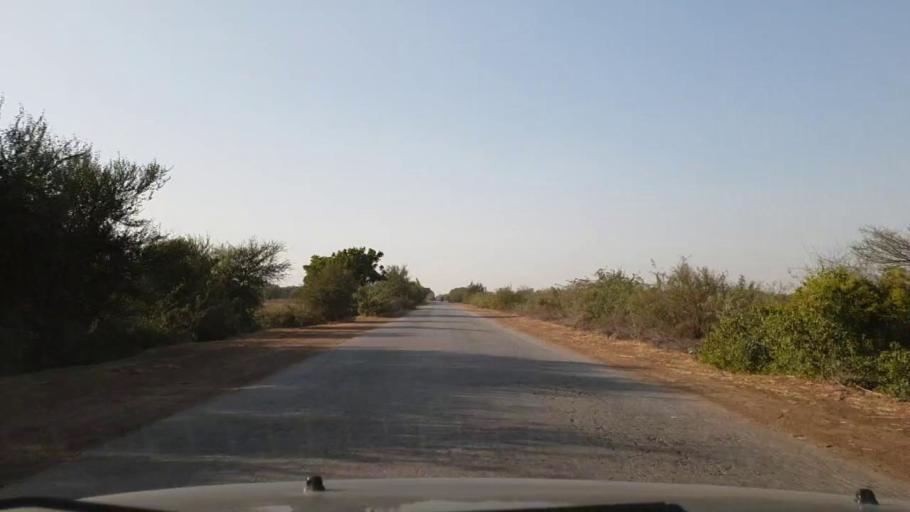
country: PK
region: Sindh
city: Tando Ghulam Ali
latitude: 25.1906
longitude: 68.8088
